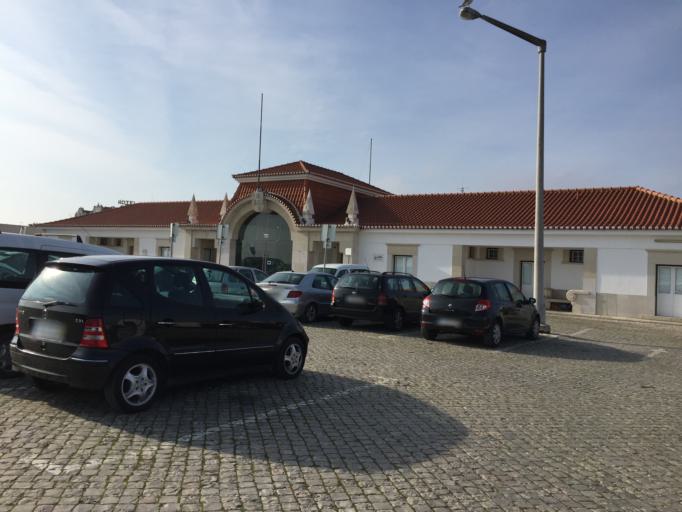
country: PT
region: Faro
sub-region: Vila Real de Santo Antonio
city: Vila Real de Santo Antonio
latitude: 37.1972
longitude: -7.4141
